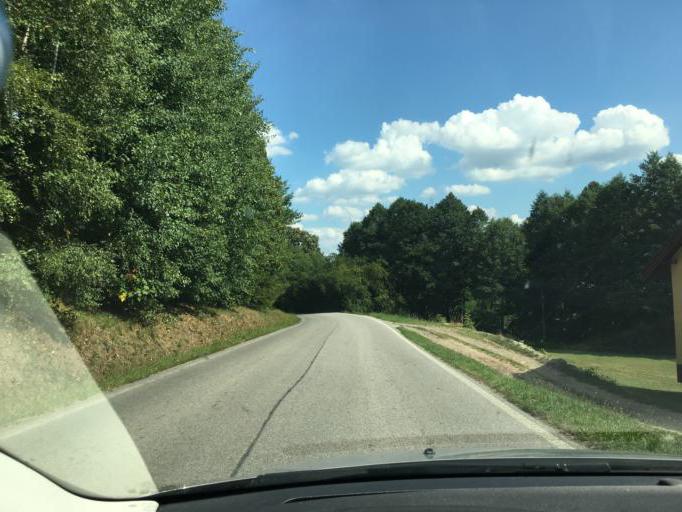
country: CZ
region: Liberecky
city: Zelezny Brod
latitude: 50.6067
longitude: 15.2850
